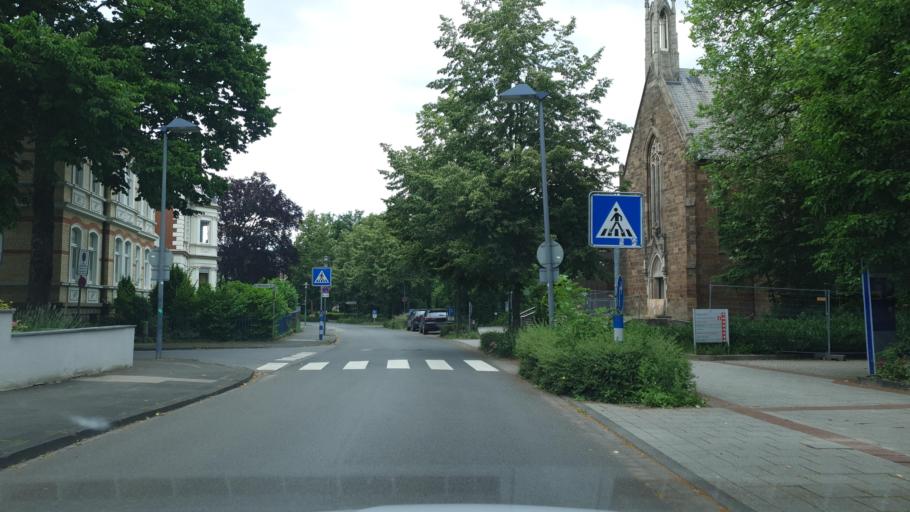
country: DE
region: North Rhine-Westphalia
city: Bad Oeynhausen
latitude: 52.2013
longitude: 8.7919
